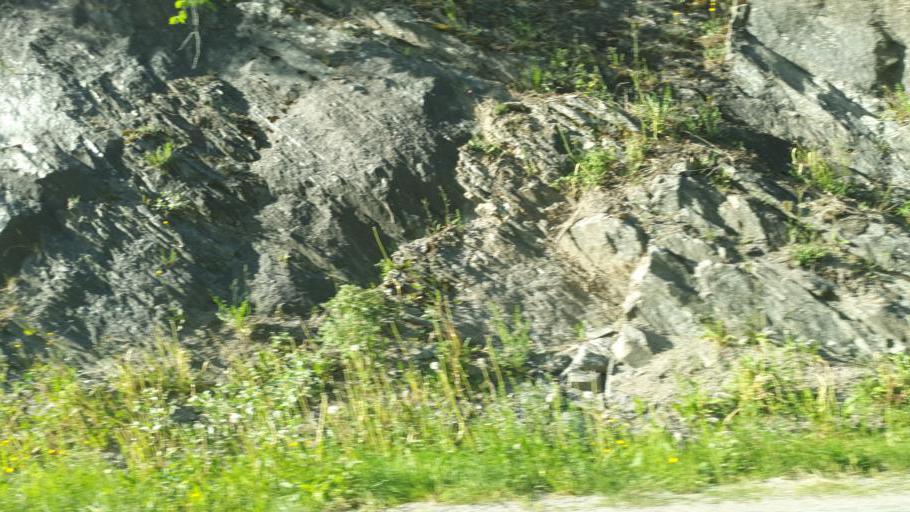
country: NO
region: Sor-Trondelag
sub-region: Rissa
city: Rissa
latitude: 63.4966
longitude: 10.1000
